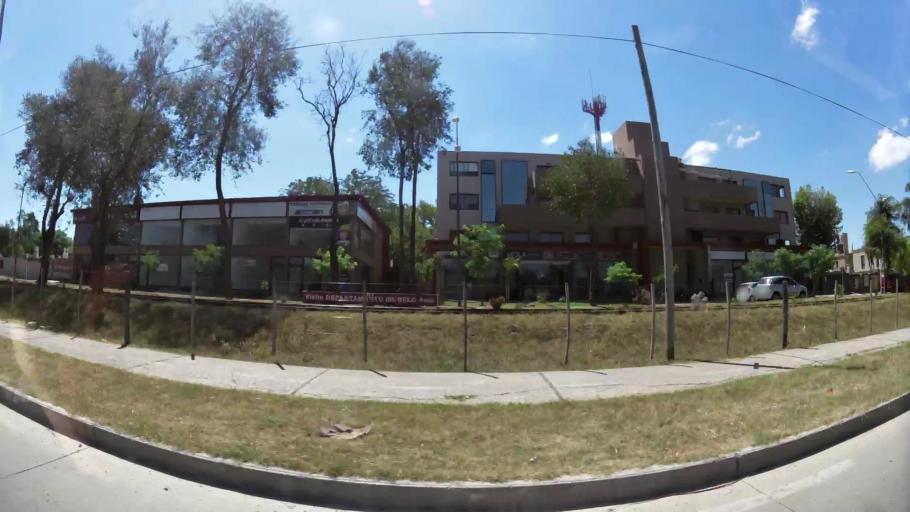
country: AR
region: Cordoba
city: Villa Allende
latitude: -31.3352
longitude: -64.2646
